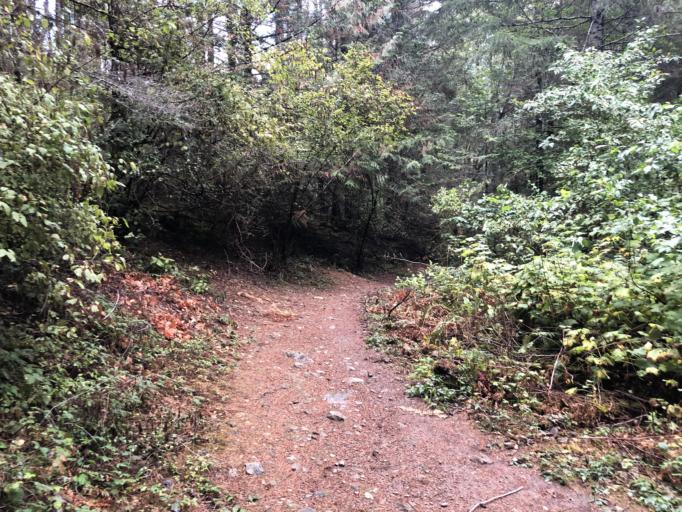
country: CA
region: British Columbia
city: Langford
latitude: 48.4722
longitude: -123.4910
